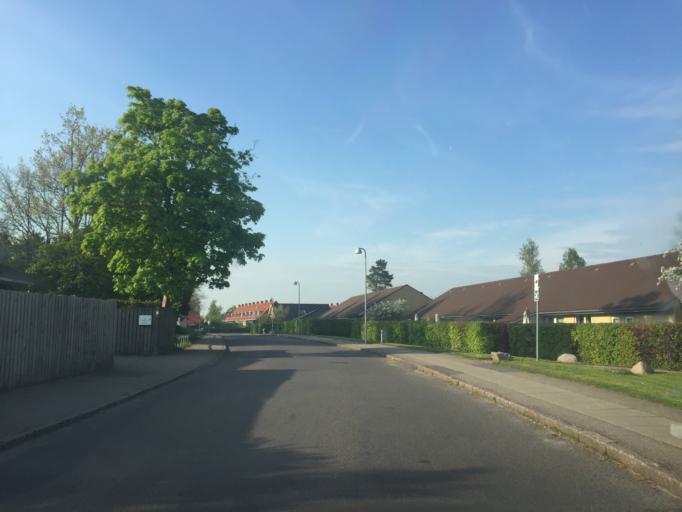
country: DK
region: Capital Region
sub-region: Hoje-Taastrup Kommune
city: Taastrup
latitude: 55.6452
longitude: 12.3086
